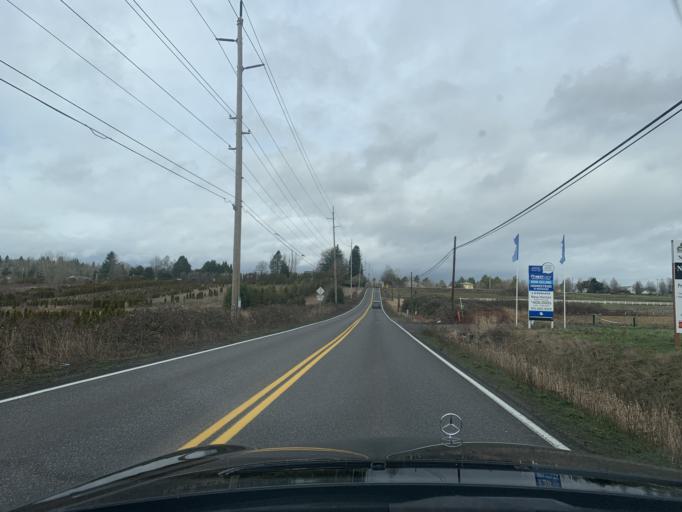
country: US
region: Oregon
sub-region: Multnomah County
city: Gresham
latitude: 45.4685
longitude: -122.4668
